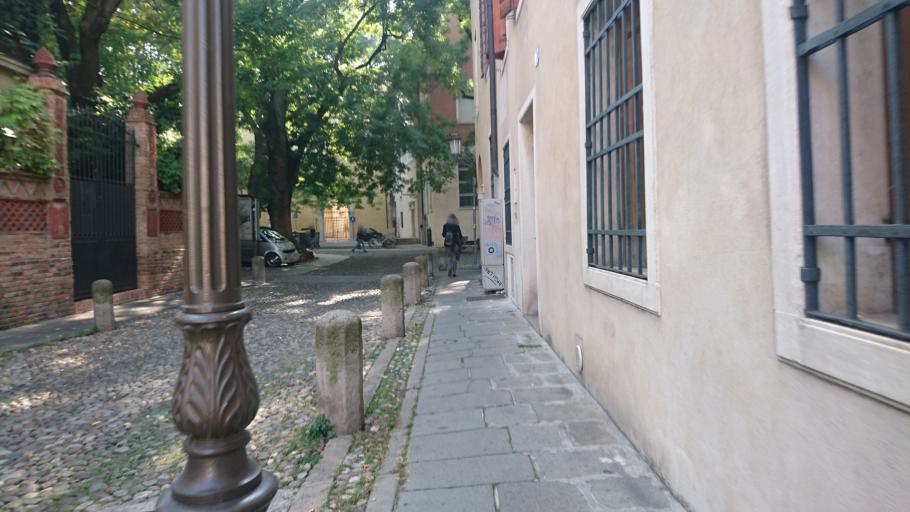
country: IT
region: Veneto
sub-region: Provincia di Padova
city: Padova
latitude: 45.4083
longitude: 11.8720
